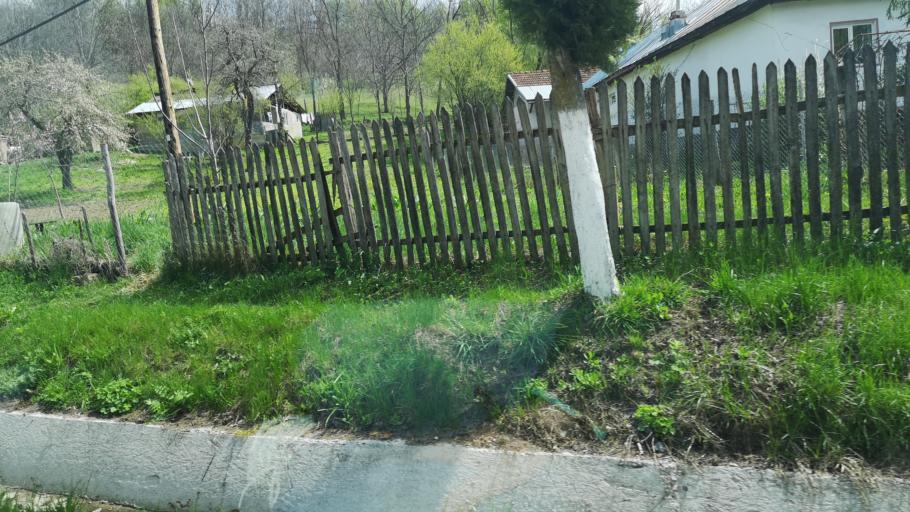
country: RO
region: Prahova
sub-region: Comuna Soimari
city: Soimari
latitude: 45.1741
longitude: 26.2118
